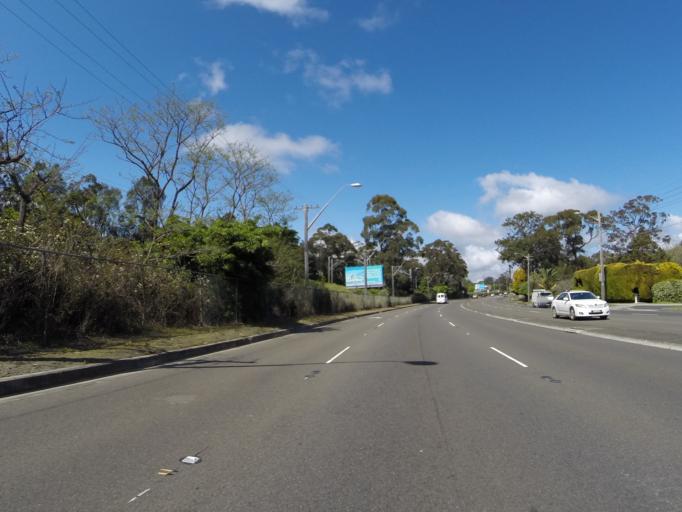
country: AU
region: New South Wales
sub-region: Sutherland Shire
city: Heathcote
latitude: -34.0826
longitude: 151.0113
